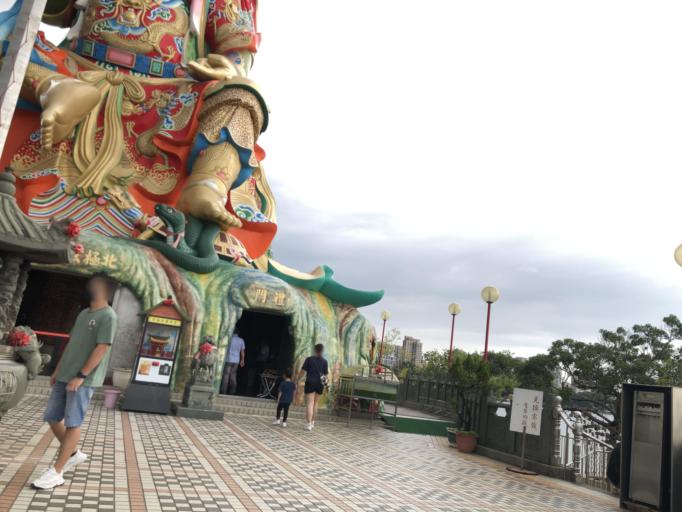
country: TW
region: Kaohsiung
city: Kaohsiung
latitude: 22.6845
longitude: 120.2962
